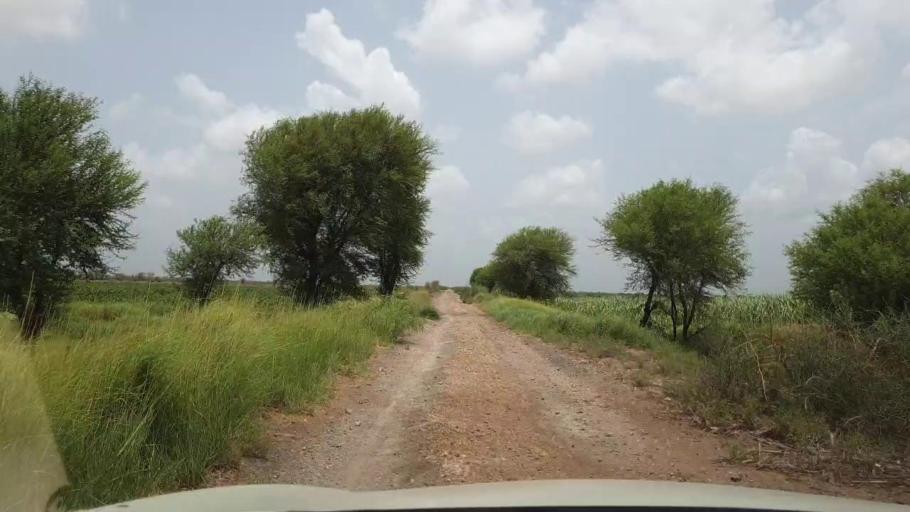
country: PK
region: Sindh
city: Chambar
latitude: 25.2185
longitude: 68.7595
